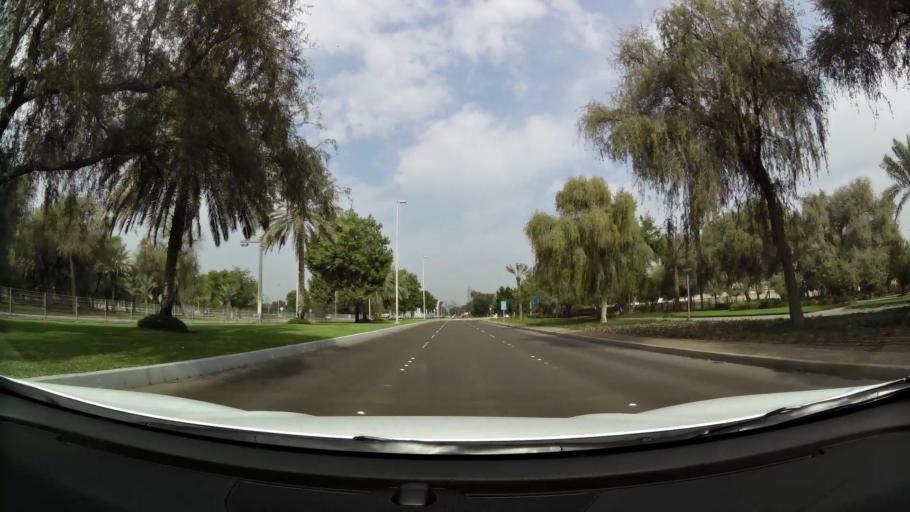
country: AE
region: Abu Dhabi
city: Abu Dhabi
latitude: 24.4508
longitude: 54.3804
